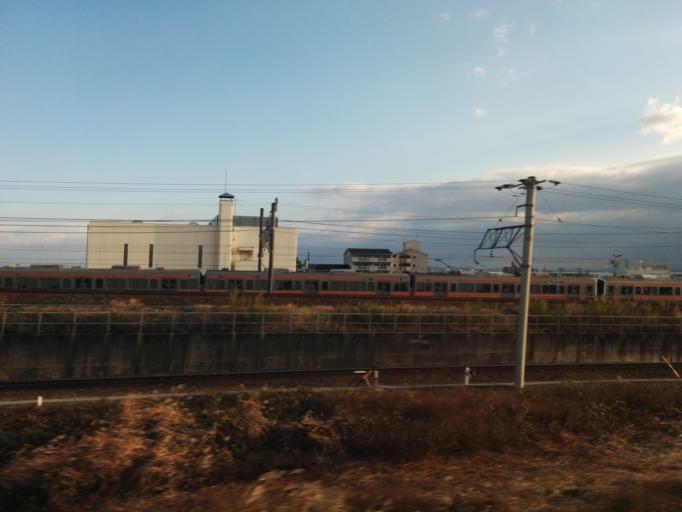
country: JP
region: Aichi
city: Nagoya-shi
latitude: 35.2027
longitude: 136.8563
